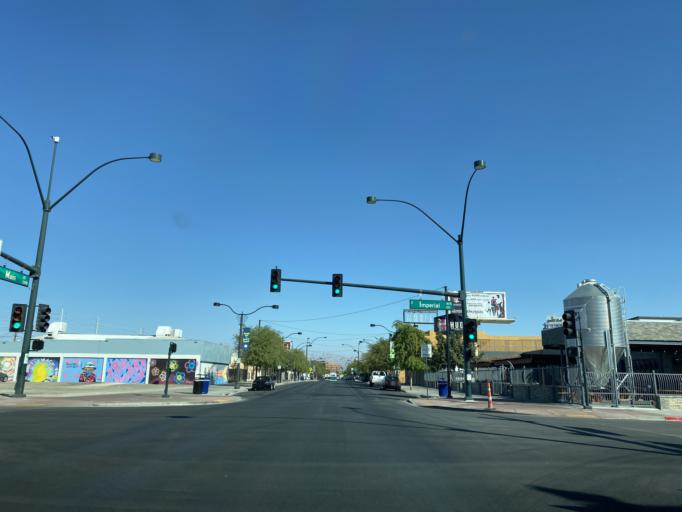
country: US
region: Nevada
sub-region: Clark County
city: Las Vegas
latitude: 36.1546
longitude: -115.1539
